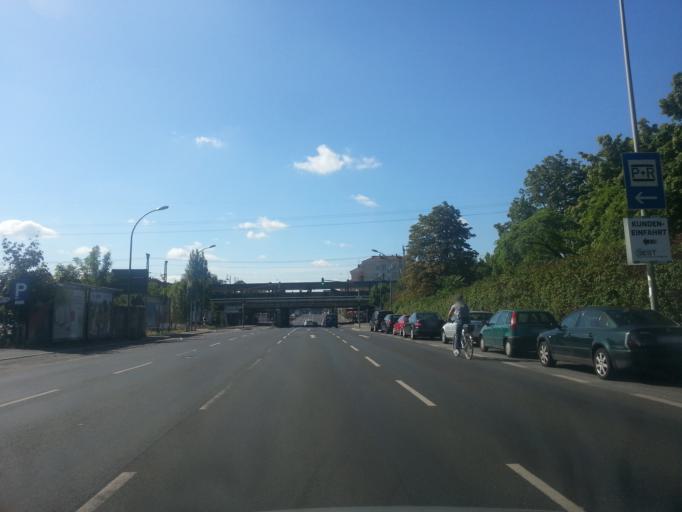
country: DE
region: Hesse
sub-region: Regierungsbezirk Darmstadt
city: Offenbach
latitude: 50.1042
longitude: 8.7839
